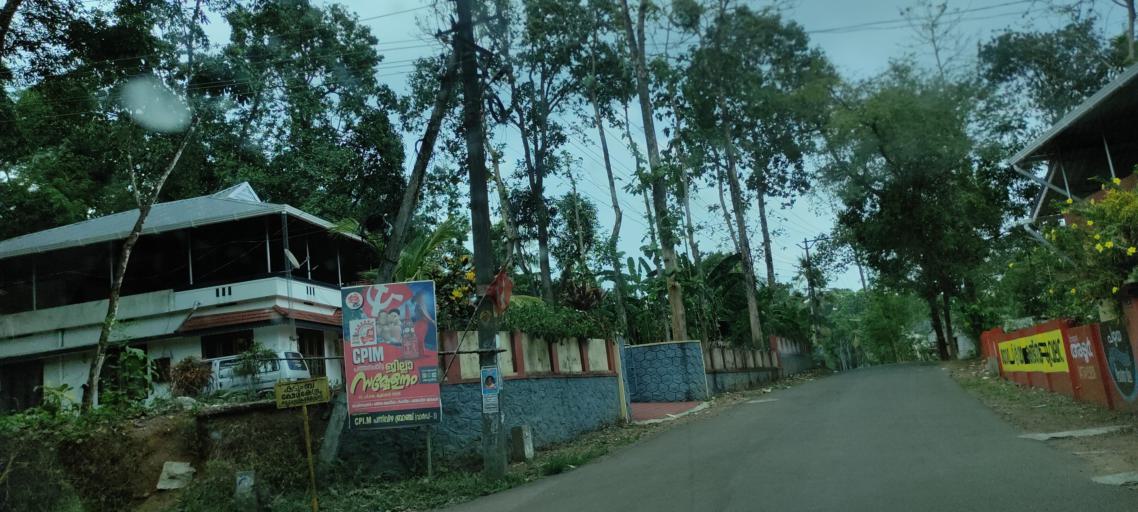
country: IN
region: Kerala
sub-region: Pattanamtitta
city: Adur
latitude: 9.1701
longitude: 76.7363
